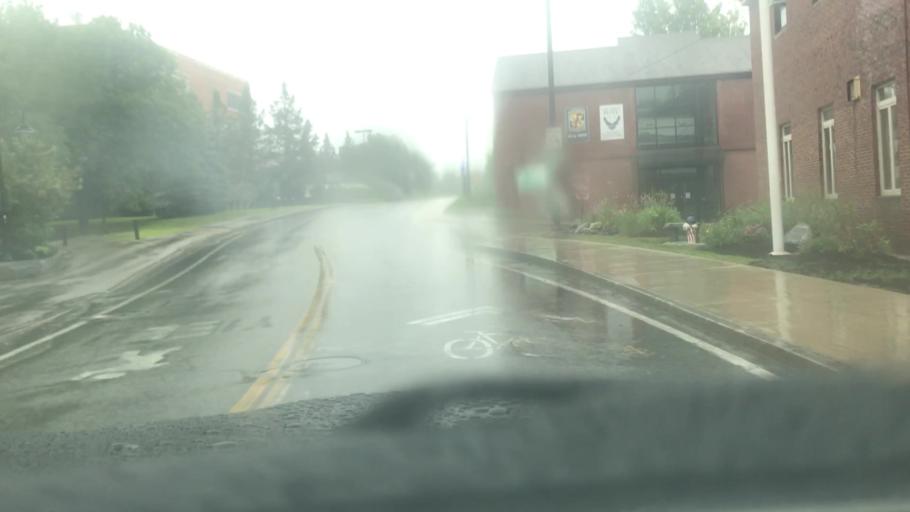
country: US
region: New Hampshire
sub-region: Strafford County
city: Durham
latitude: 43.1359
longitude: -70.9359
